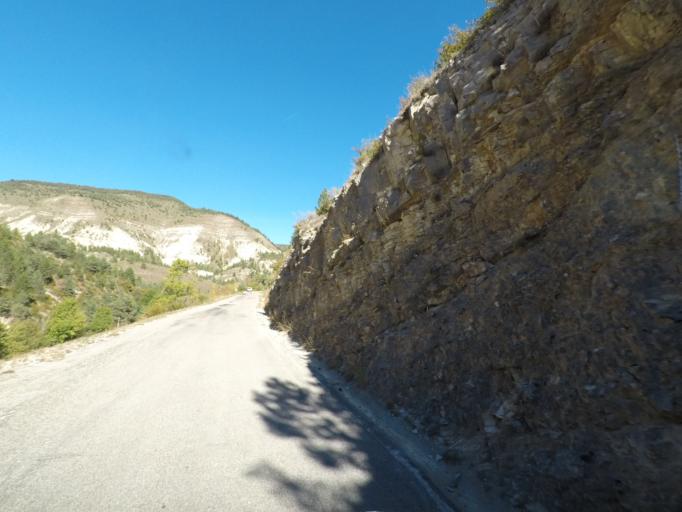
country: FR
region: Rhone-Alpes
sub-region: Departement de la Drome
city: Die
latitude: 44.5144
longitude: 5.3458
